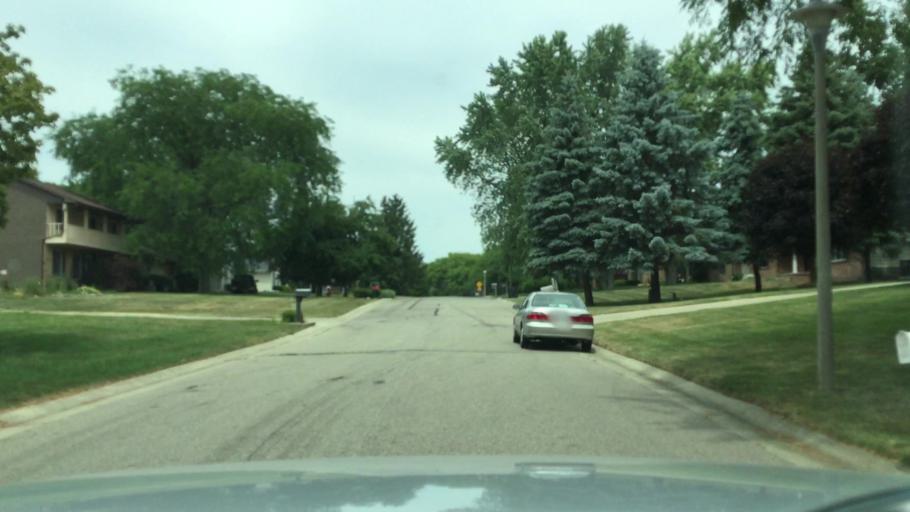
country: US
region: Michigan
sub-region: Genesee County
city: Flushing
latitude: 43.0239
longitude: -83.7991
